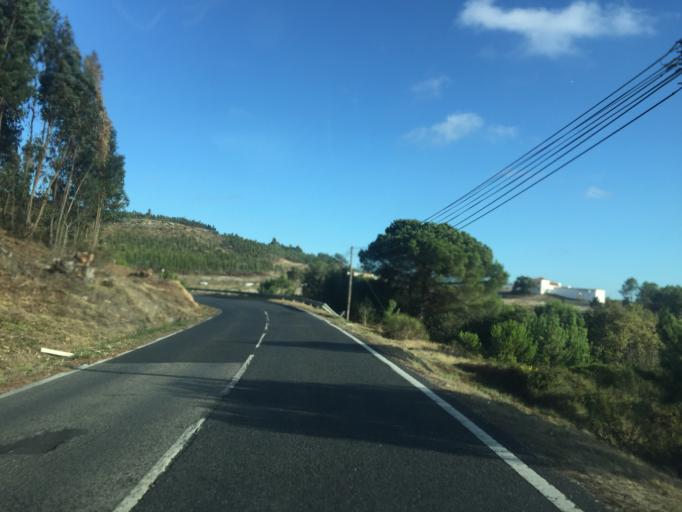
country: PT
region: Lisbon
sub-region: Torres Vedras
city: Torres Vedras
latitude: 39.1295
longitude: -9.2633
